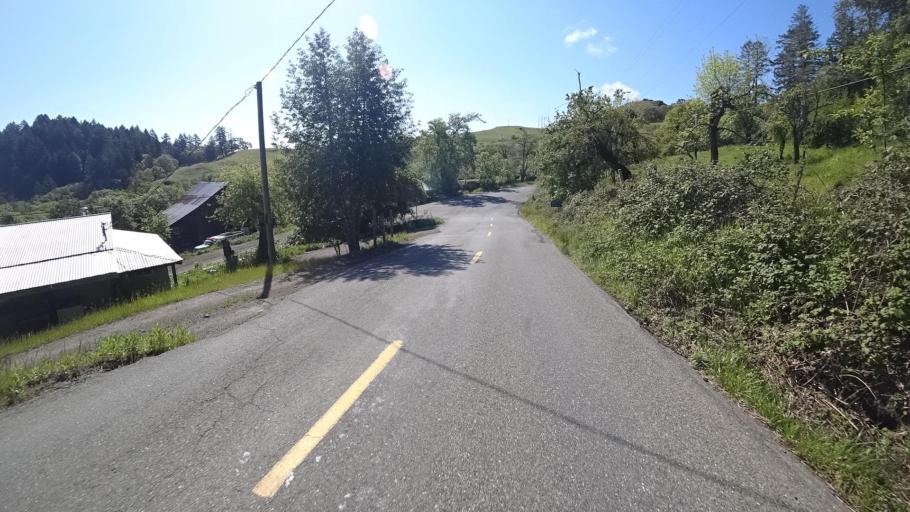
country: US
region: California
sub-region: Humboldt County
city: Redway
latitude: 40.0844
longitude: -123.6596
